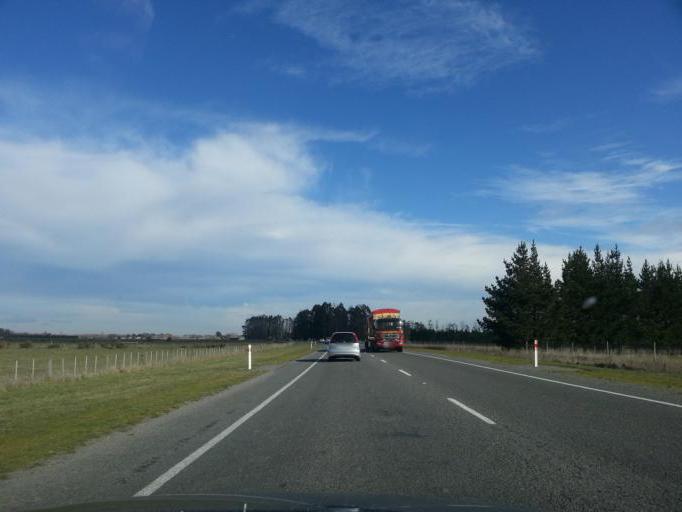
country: NZ
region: Canterbury
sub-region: Waimakariri District
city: Kaiapoi
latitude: -43.3580
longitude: 172.6558
